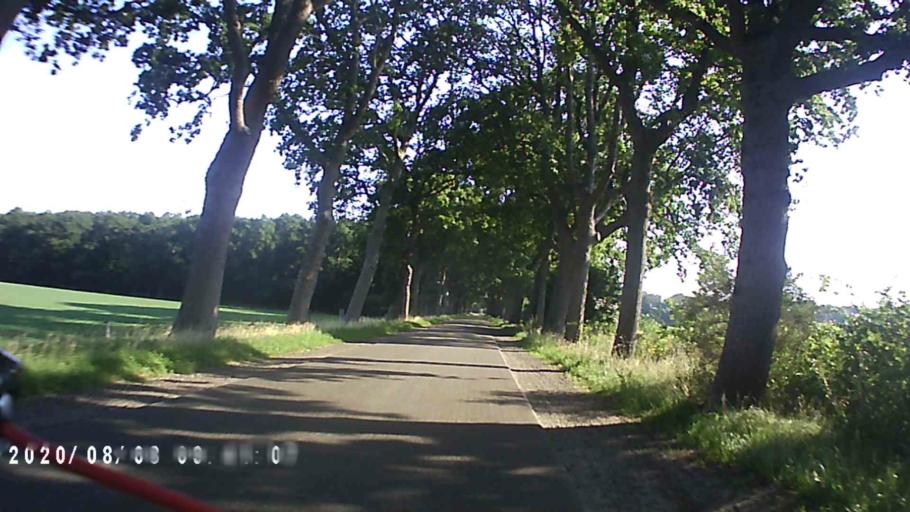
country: NL
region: Groningen
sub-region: Gemeente Leek
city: Leek
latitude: 53.0639
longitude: 6.3984
